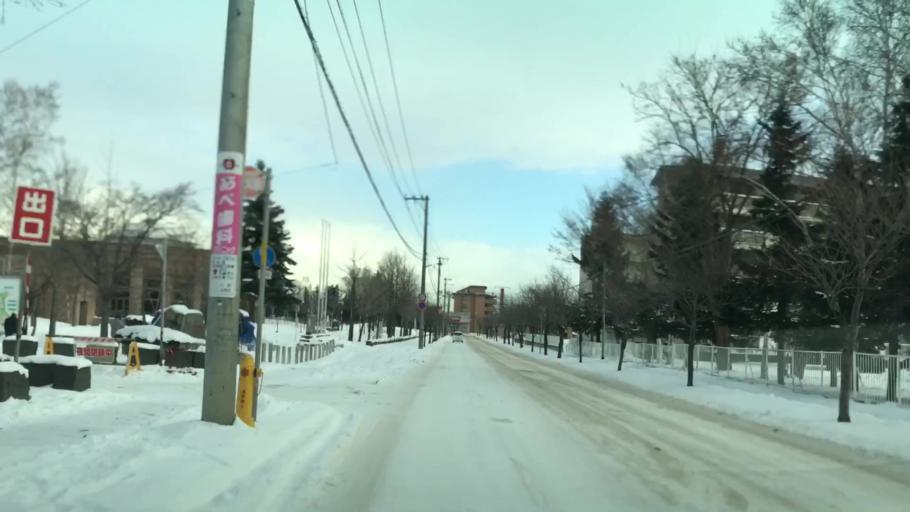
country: JP
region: Hokkaido
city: Sapporo
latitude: 43.0901
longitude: 141.3048
